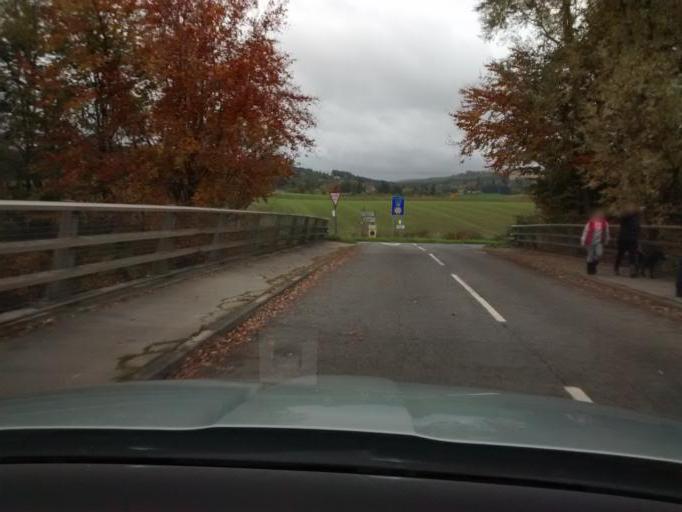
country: GB
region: Scotland
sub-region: Perth and Kinross
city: Auchterarder
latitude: 56.2954
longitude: -3.6879
